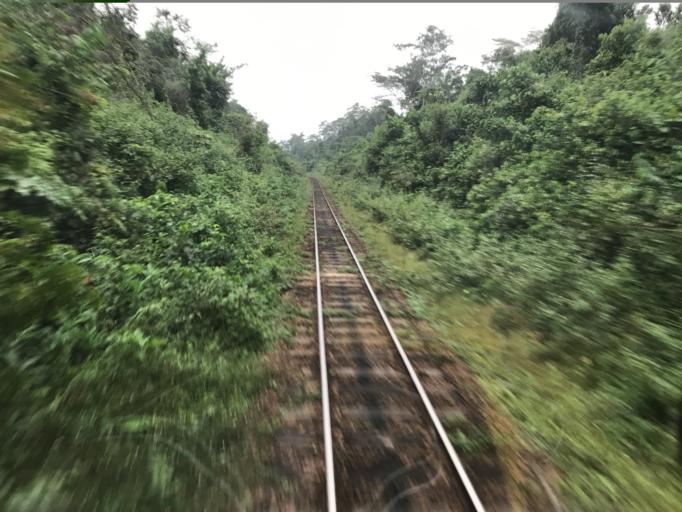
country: CM
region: Littoral
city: Edea
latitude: 3.9631
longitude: 10.0832
